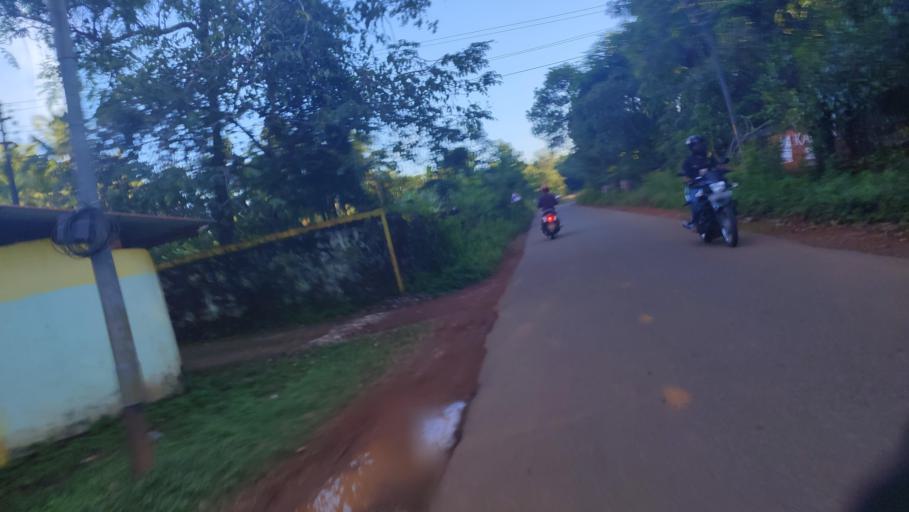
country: IN
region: Kerala
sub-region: Kasaragod District
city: Kannangad
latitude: 12.4129
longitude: 75.0953
